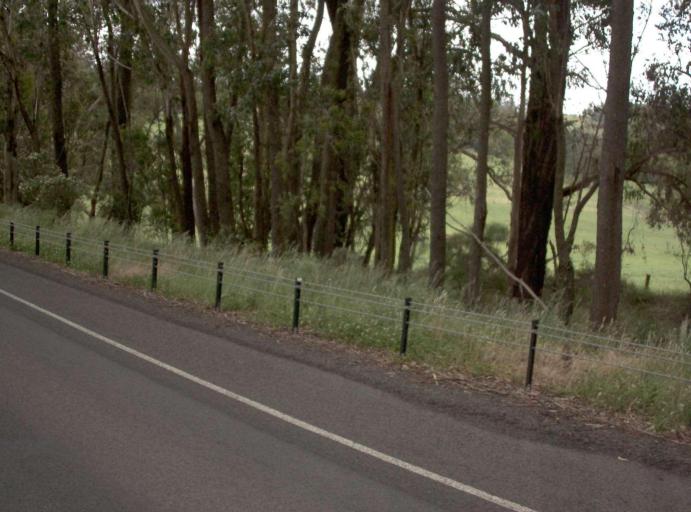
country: AU
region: Victoria
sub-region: Baw Baw
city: Warragul
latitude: -38.0745
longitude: 145.9652
